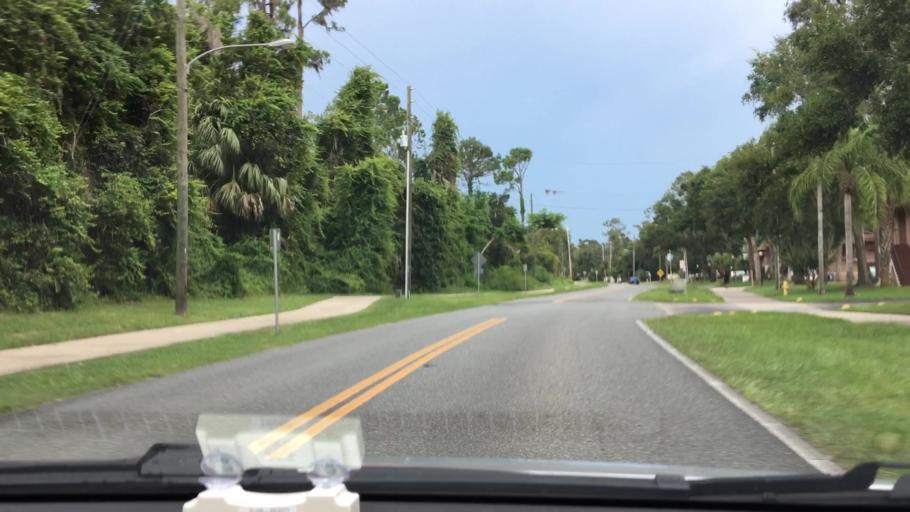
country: US
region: Florida
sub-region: Volusia County
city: Deltona
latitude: 28.8659
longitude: -81.2550
